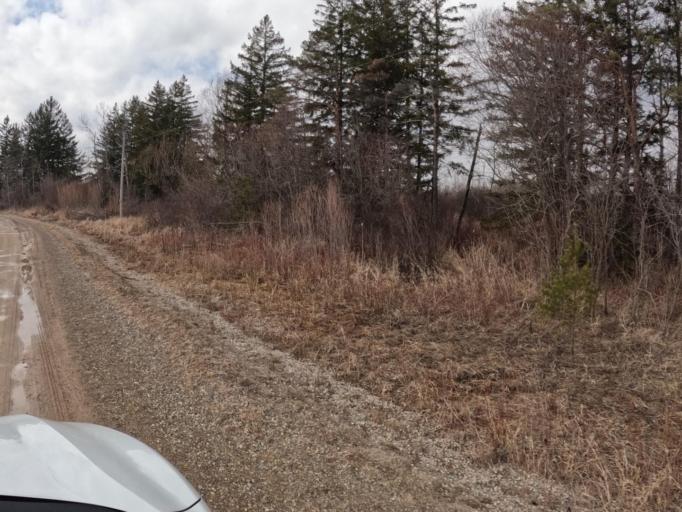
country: CA
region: Ontario
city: Shelburne
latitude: 44.0332
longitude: -80.2350
